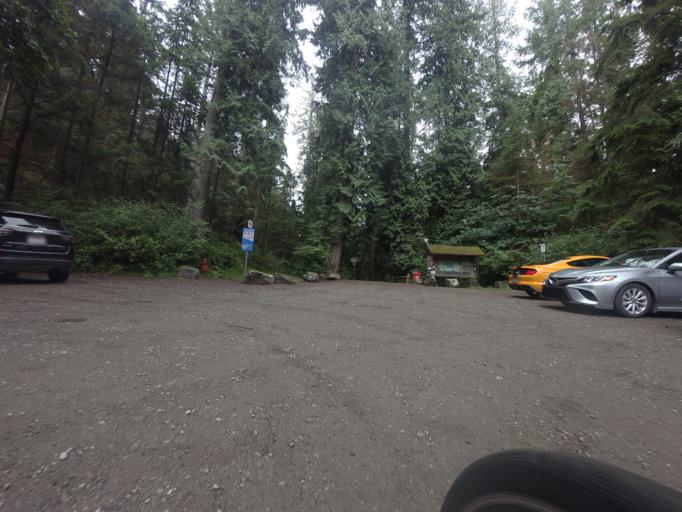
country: CA
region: British Columbia
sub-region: Greater Vancouver Regional District
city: Bowen Island
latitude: 49.3372
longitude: -123.2629
